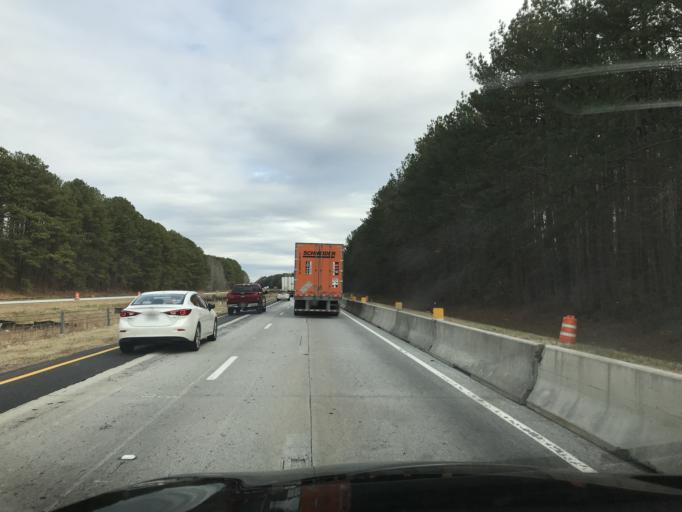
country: US
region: Georgia
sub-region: Carroll County
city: Temple
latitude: 33.7167
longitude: -84.9940
